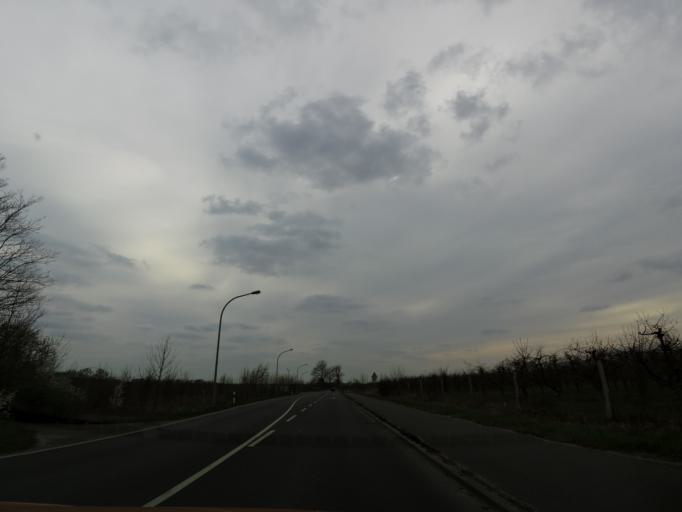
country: DE
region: Brandenburg
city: Mullrose
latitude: 52.2915
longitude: 14.4656
